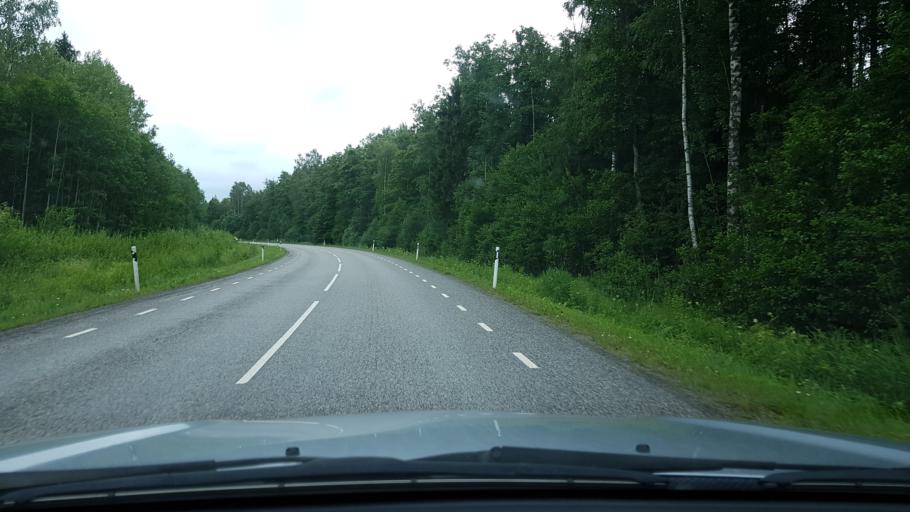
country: EE
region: Ida-Virumaa
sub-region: Narva-Joesuu linn
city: Narva-Joesuu
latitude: 59.3570
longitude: 27.9268
